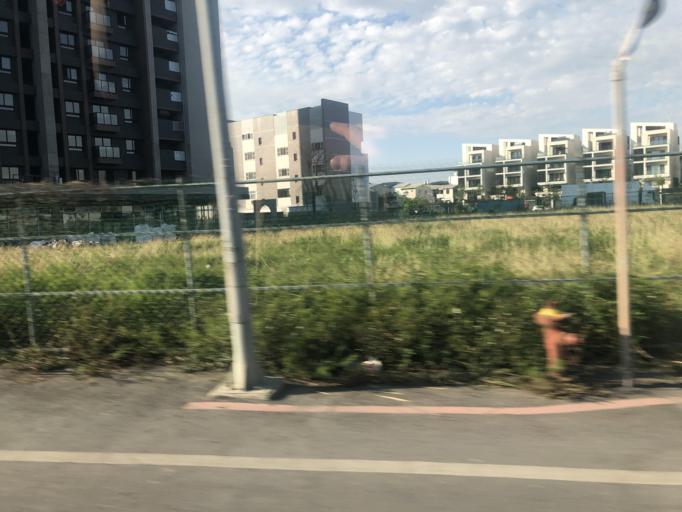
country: TW
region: Taiwan
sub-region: Tainan
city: Tainan
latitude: 23.0302
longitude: 120.1955
